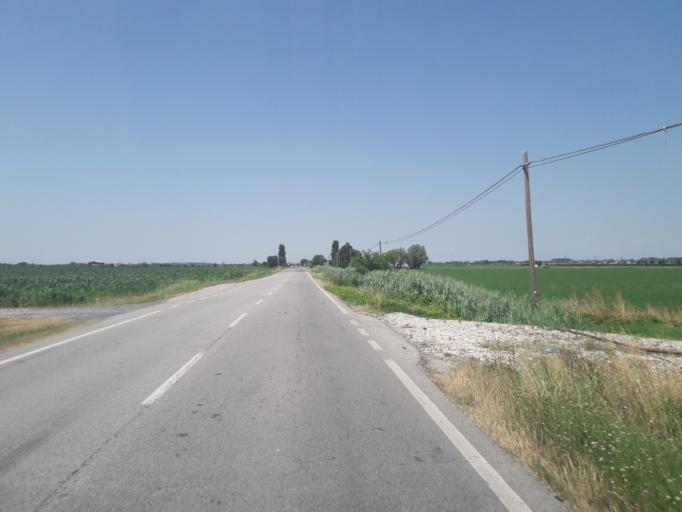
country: IT
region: Veneto
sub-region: Provincia di Rovigo
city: Papozze
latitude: 45.0054
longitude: 12.1702
